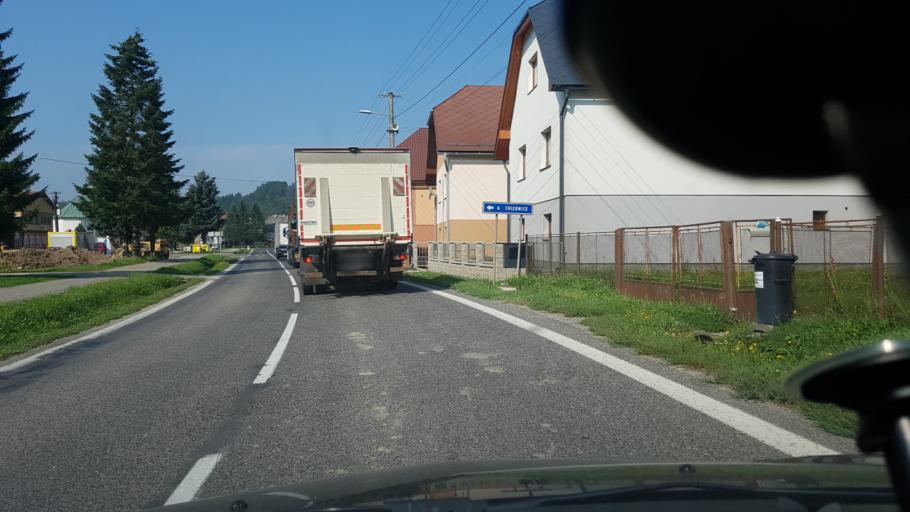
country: SK
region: Zilinsky
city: Tvrdosin
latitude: 49.2664
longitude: 19.4466
